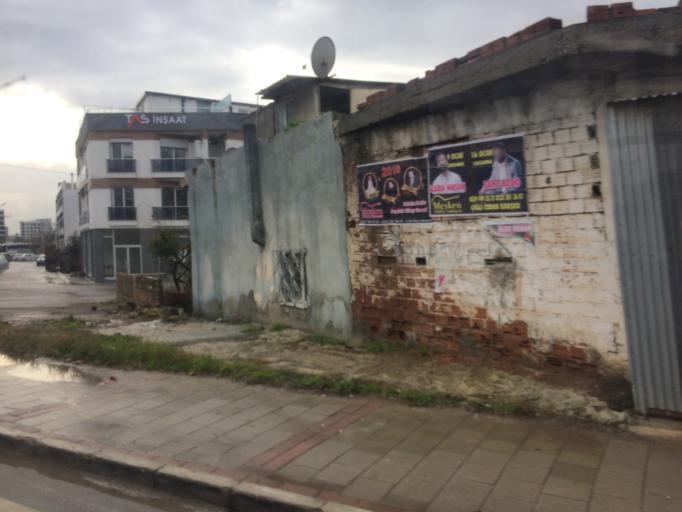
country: TR
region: Izmir
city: Karsiyaka
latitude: 38.5171
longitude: 27.0414
